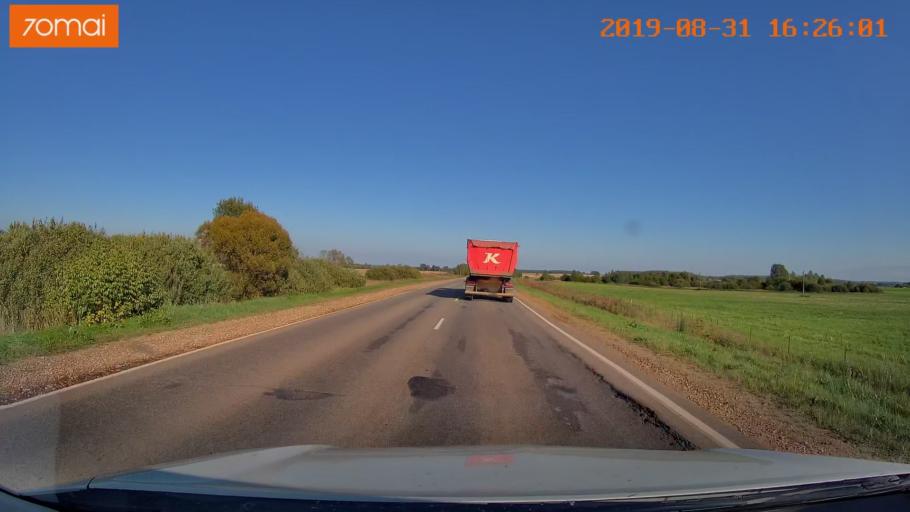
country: RU
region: Kaluga
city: Babynino
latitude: 54.5190
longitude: 35.7247
